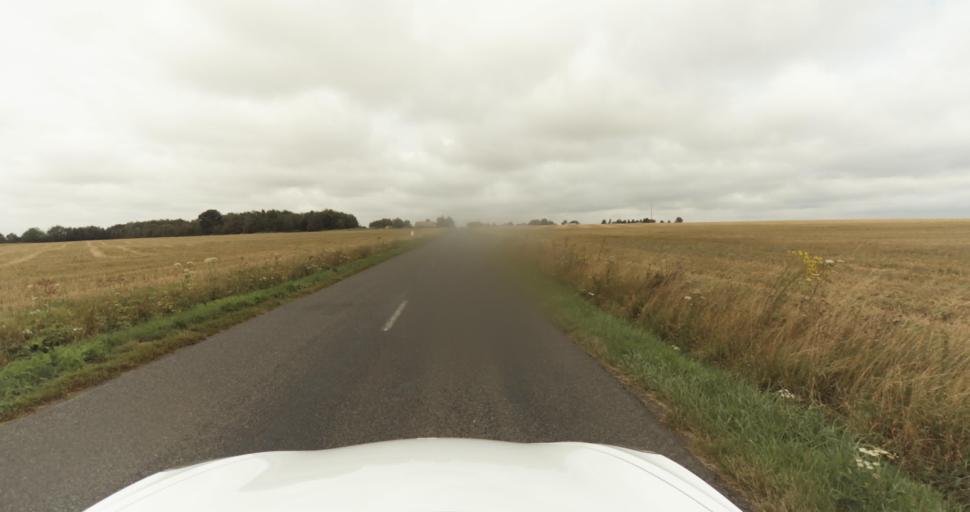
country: FR
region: Haute-Normandie
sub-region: Departement de l'Eure
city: Aviron
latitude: 49.0608
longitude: 1.0782
